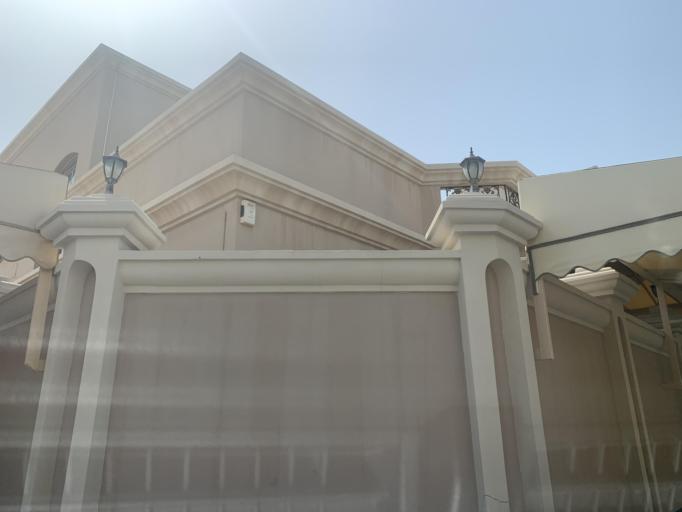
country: BH
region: Northern
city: Ar Rifa'
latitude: 26.1432
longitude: 50.5695
